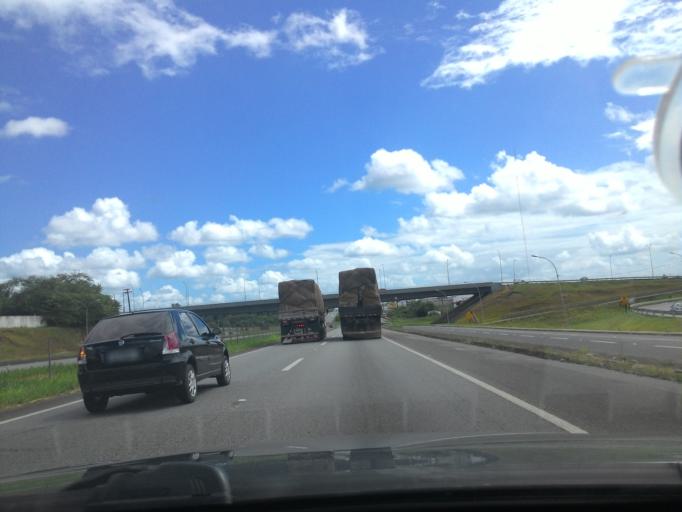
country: BR
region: Sao Paulo
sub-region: Registro
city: Registro
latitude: -24.5071
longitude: -47.8488
